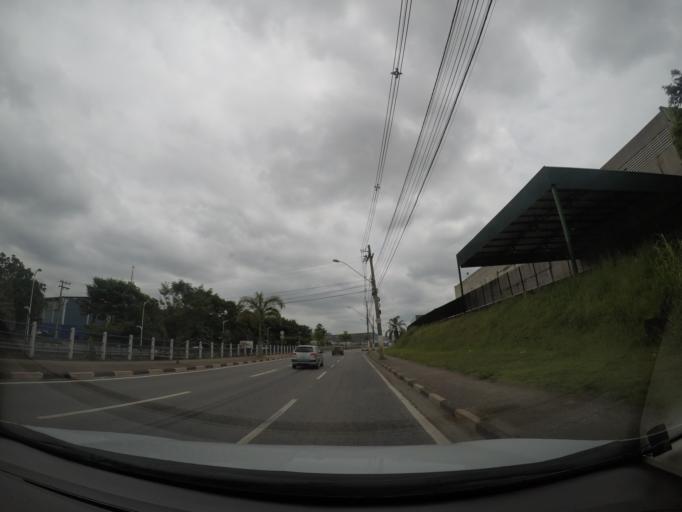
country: BR
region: Sao Paulo
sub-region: Aruja
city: Aruja
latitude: -23.4017
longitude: -46.3481
